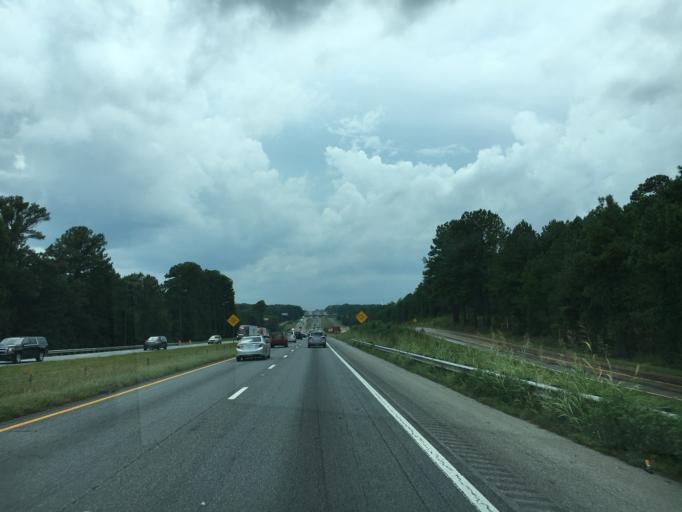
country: US
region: South Carolina
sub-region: Spartanburg County
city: Cowpens
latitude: 35.0347
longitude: -81.8437
